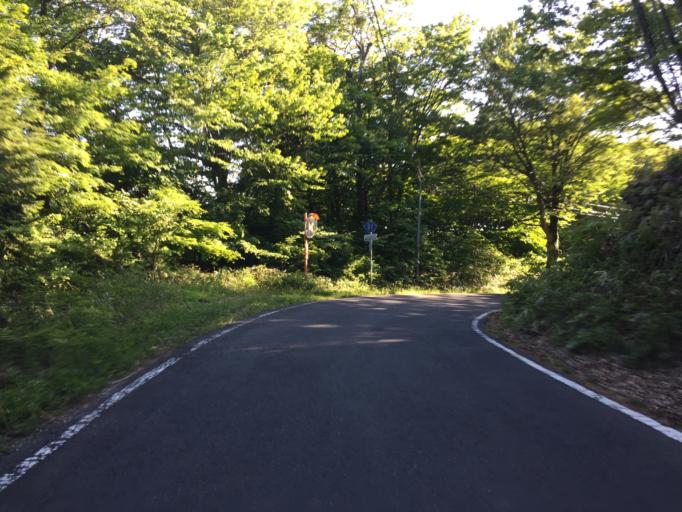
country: JP
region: Ibaraki
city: Kitaibaraki
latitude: 36.9045
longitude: 140.5895
